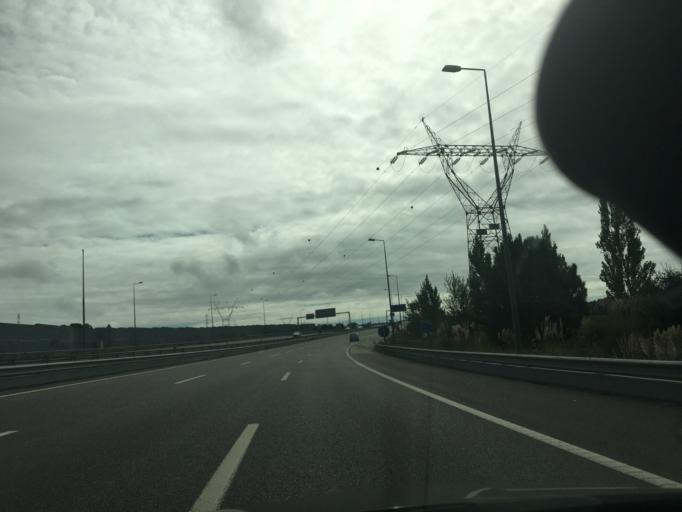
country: PT
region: Porto
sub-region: Matosinhos
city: Guifoes
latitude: 41.2094
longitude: -8.6520
